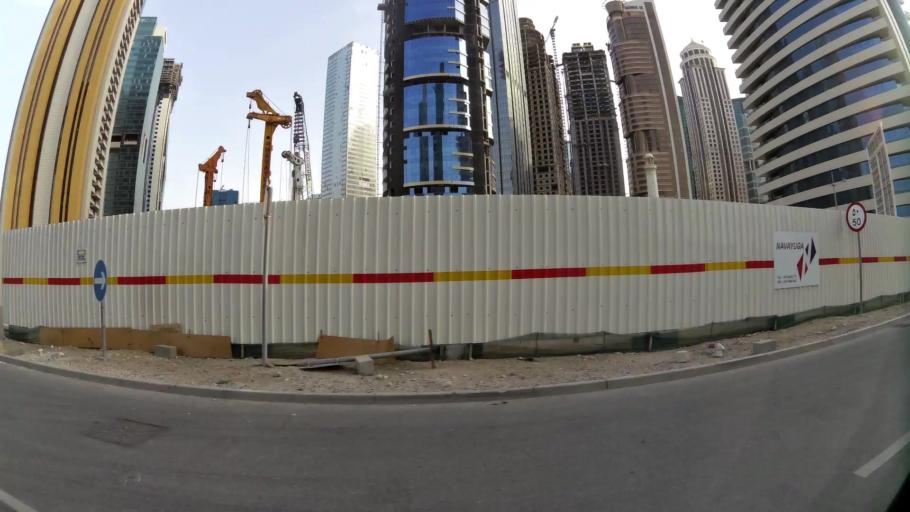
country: QA
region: Baladiyat ad Dawhah
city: Doha
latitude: 25.3304
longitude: 51.5344
